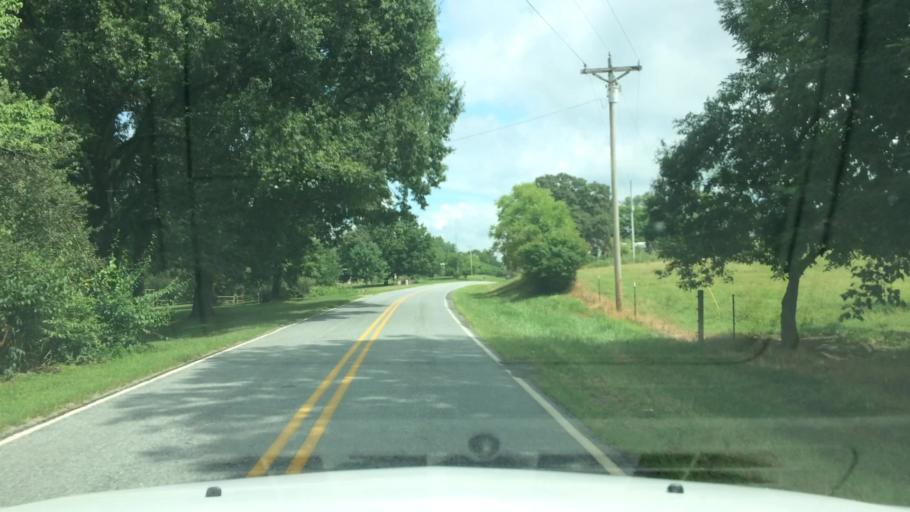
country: US
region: North Carolina
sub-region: Yadkin County
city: Jonesville
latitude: 36.1141
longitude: -80.8571
